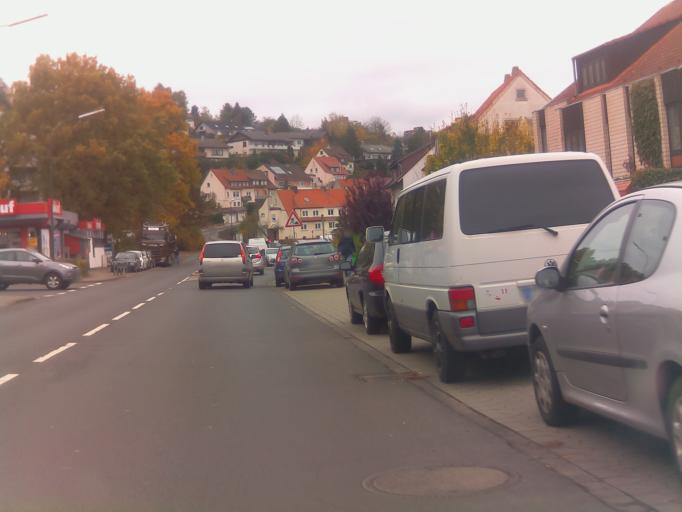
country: DE
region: Hesse
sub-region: Regierungsbezirk Kassel
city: Fulda
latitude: 50.5684
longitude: 9.6649
